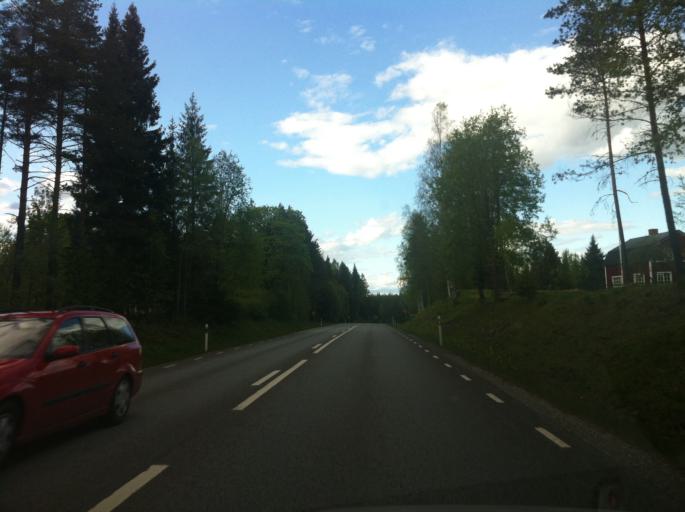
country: SE
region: Vaermland
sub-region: Filipstads Kommun
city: Filipstad
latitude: 59.7601
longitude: 14.2568
